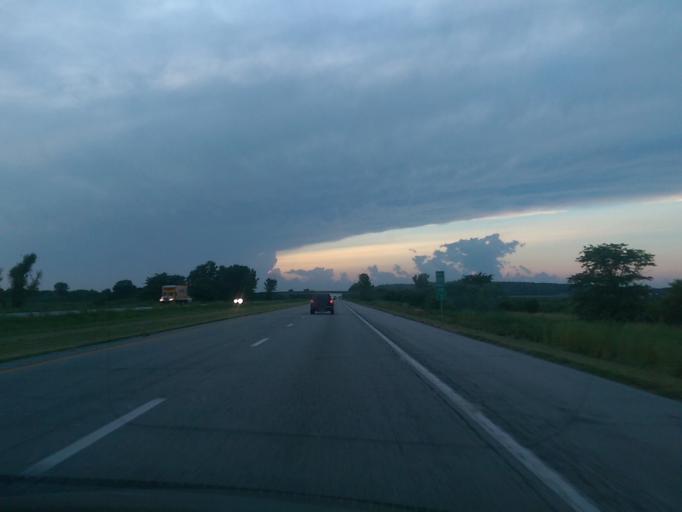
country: US
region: Iowa
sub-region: Fremont County
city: Hamburg
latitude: 40.5219
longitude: -95.6064
